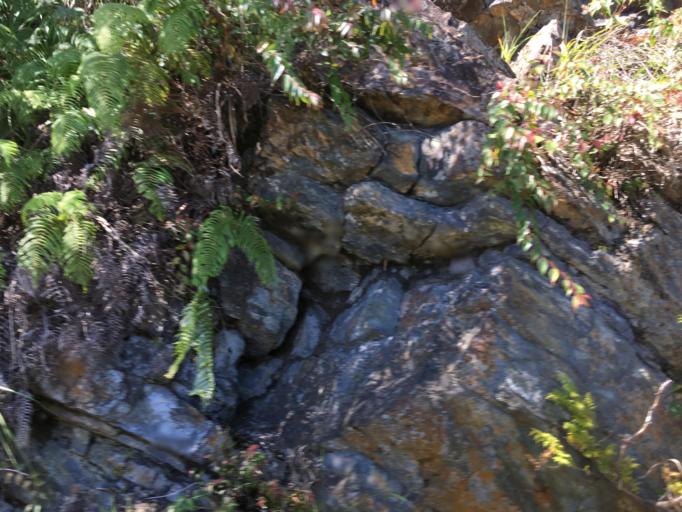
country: TW
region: Taiwan
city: Daxi
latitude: 24.5308
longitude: 121.4011
